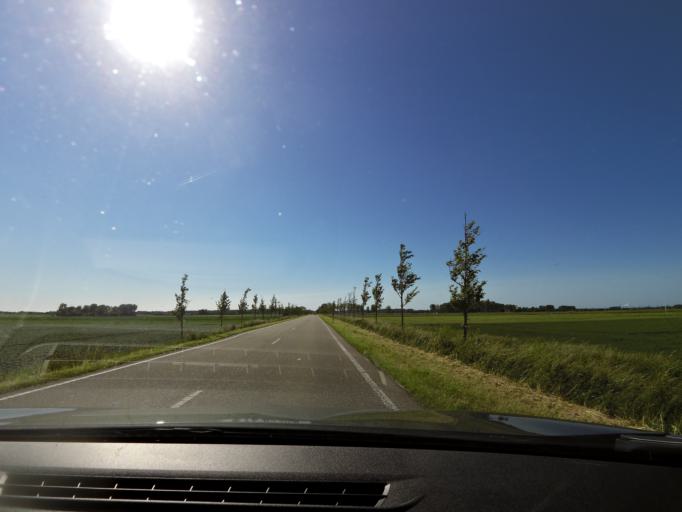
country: NL
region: South Holland
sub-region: Gemeente Hellevoetsluis
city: Nieuwenhoorn
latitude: 51.8536
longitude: 4.1298
